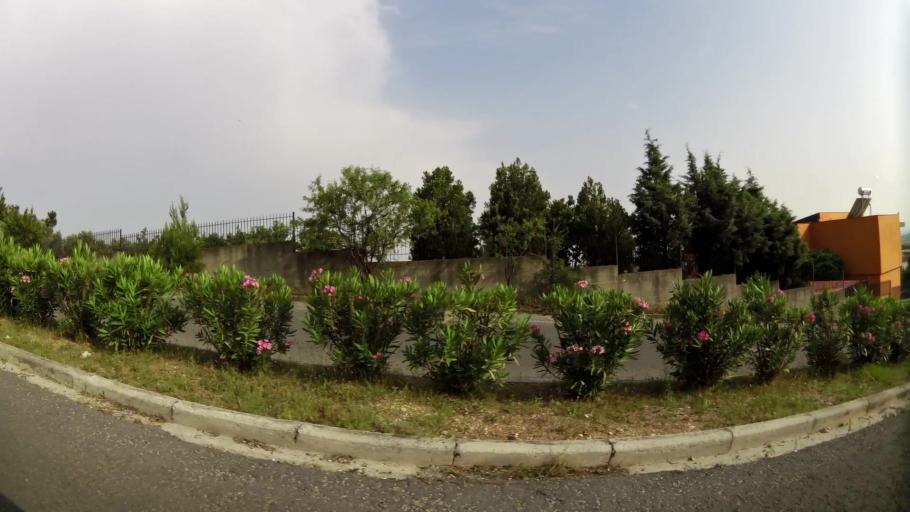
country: GR
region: Central Macedonia
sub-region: Nomos Thessalonikis
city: Oraiokastro
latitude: 40.7194
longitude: 22.9157
